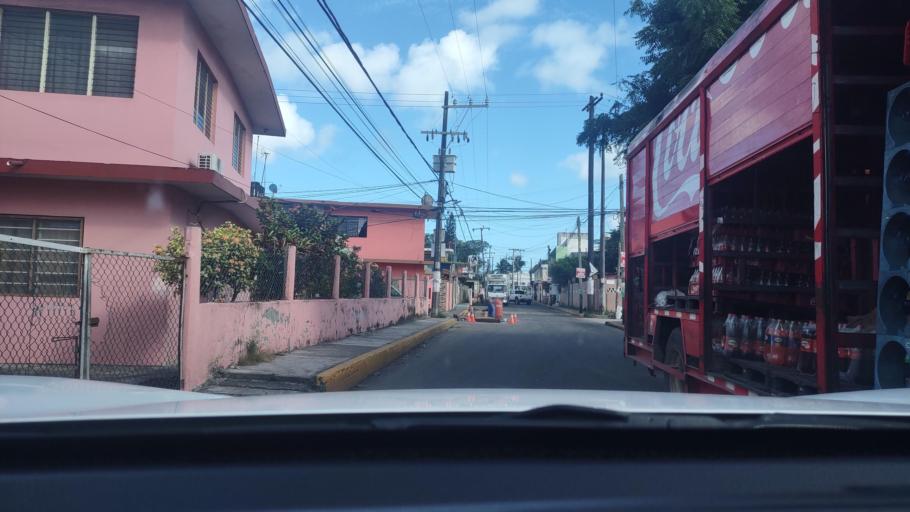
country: MX
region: Veracruz
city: El Tejar
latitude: 19.0746
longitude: -96.1629
